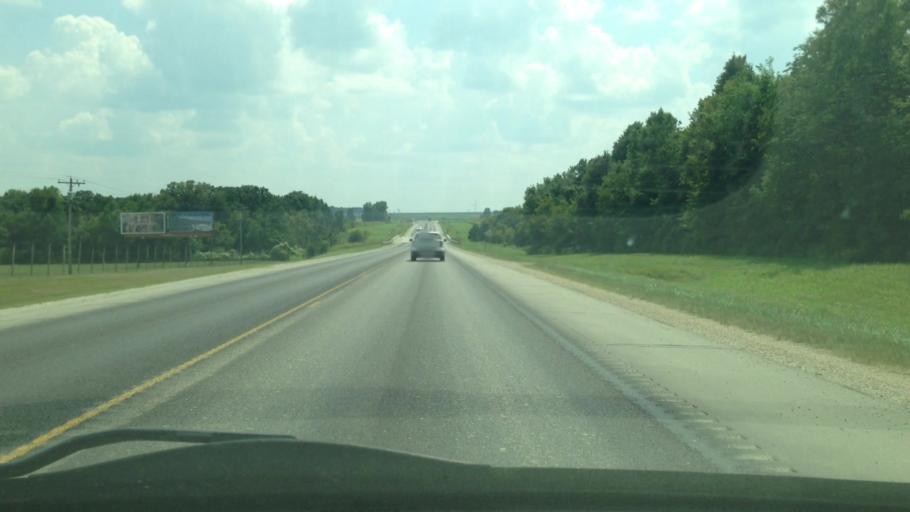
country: US
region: Minnesota
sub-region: Mower County
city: Grand Meadow
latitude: 43.7204
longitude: -92.4794
